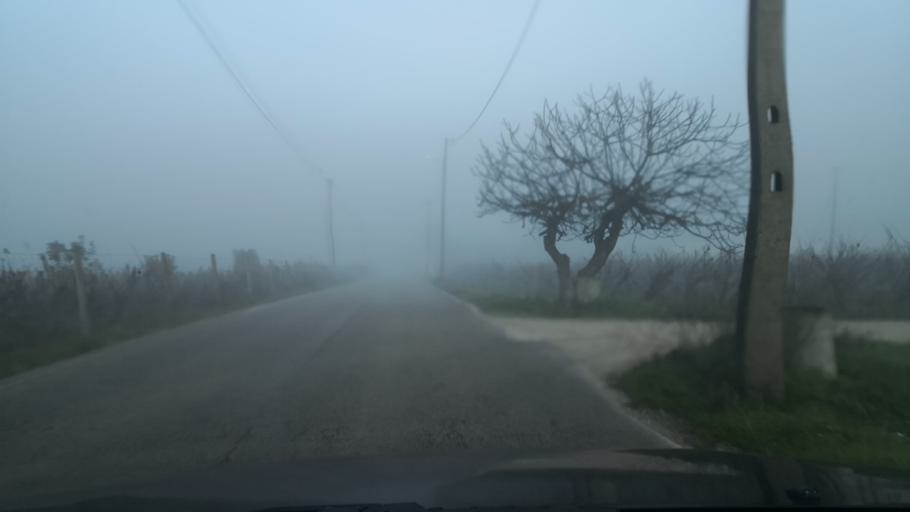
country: PT
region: Setubal
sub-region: Palmela
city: Palmela
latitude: 38.6037
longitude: -8.8493
